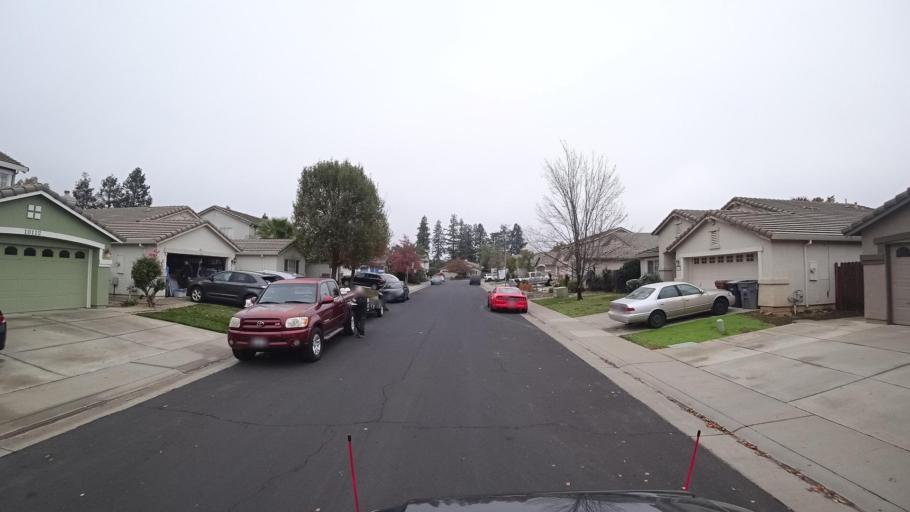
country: US
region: California
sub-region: Sacramento County
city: Elk Grove
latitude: 38.3932
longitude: -121.3644
